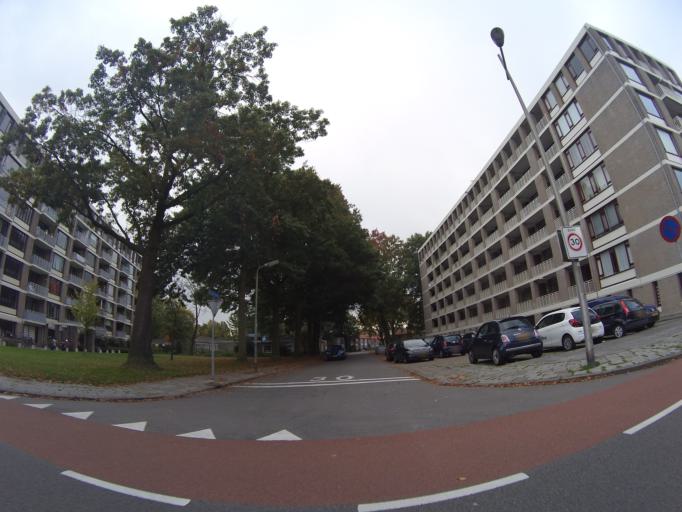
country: NL
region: Utrecht
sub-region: Gemeente Amersfoort
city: Randenbroek
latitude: 52.1502
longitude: 5.4065
